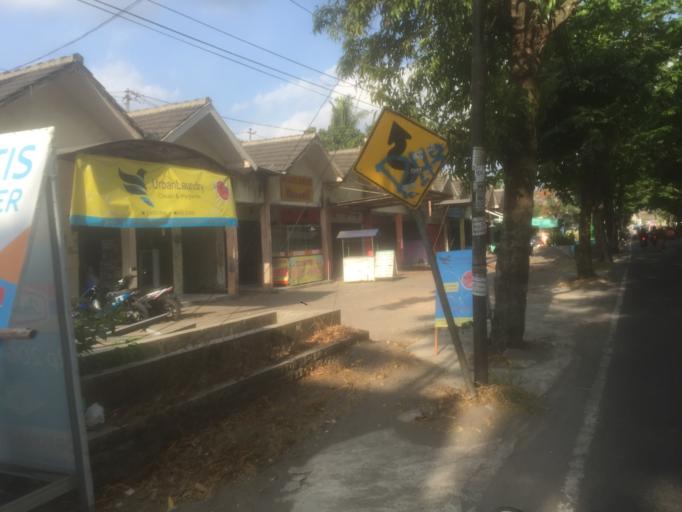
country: ID
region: Daerah Istimewa Yogyakarta
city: Melati
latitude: -7.7191
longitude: 110.3743
